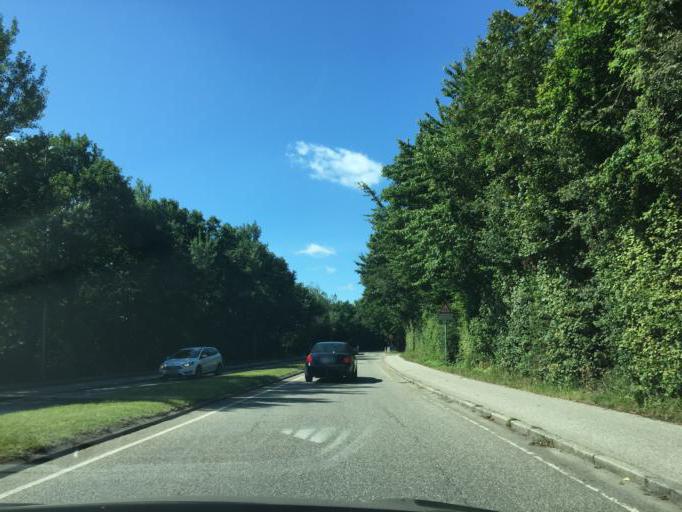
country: DK
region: South Denmark
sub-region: Odense Kommune
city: Odense
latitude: 55.3851
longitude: 10.3544
